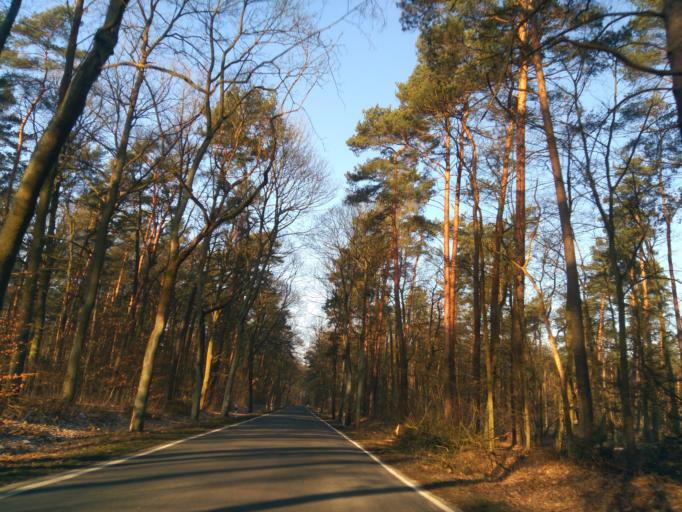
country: DE
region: Brandenburg
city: Brieselang
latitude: 52.6434
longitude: 13.0241
